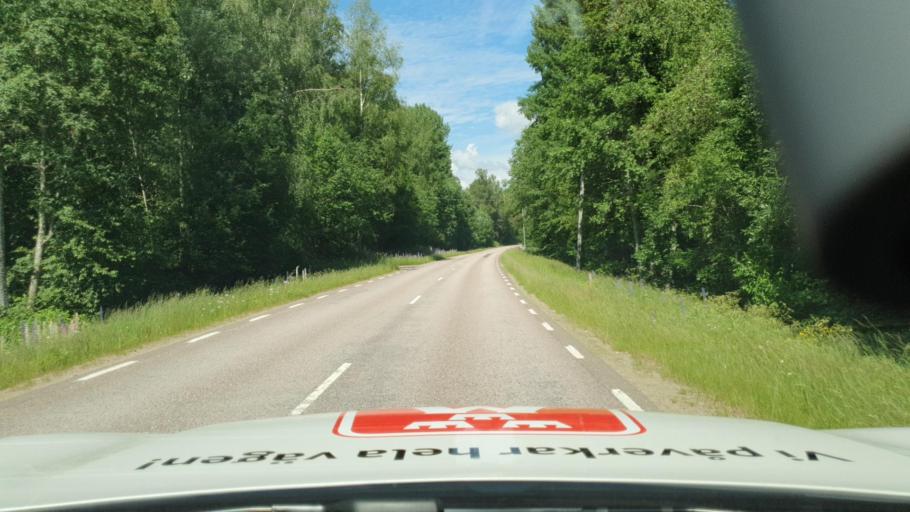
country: SE
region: Vaermland
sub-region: Torsby Kommun
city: Torsby
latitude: 60.3152
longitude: 13.0107
